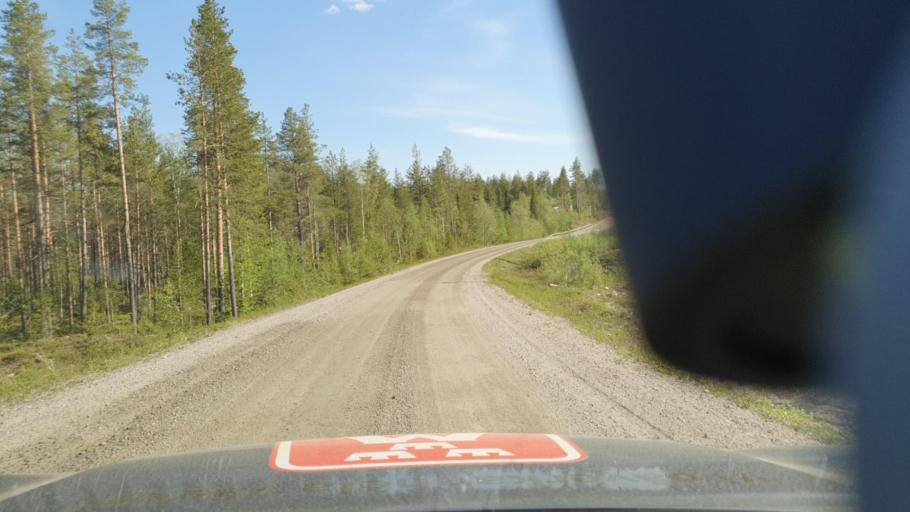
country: SE
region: Norrbotten
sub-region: Bodens Kommun
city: Boden
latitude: 66.5158
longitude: 21.9089
